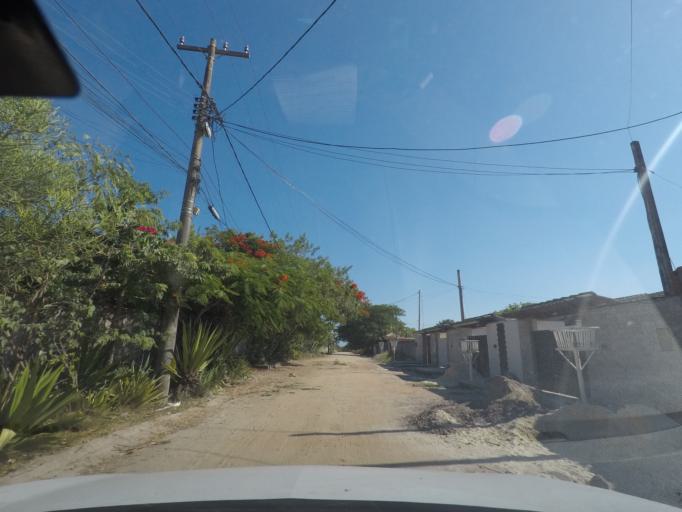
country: BR
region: Rio de Janeiro
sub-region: Marica
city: Marica
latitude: -22.9685
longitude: -42.9244
